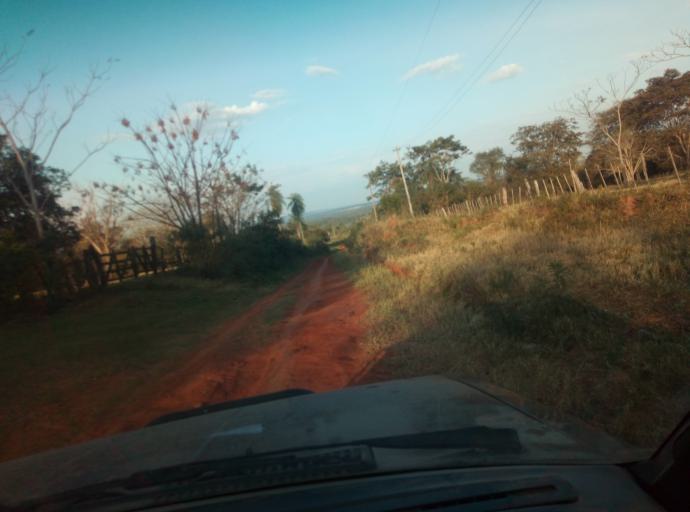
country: PY
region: Caaguazu
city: Doctor Cecilio Baez
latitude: -25.1523
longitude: -56.2457
